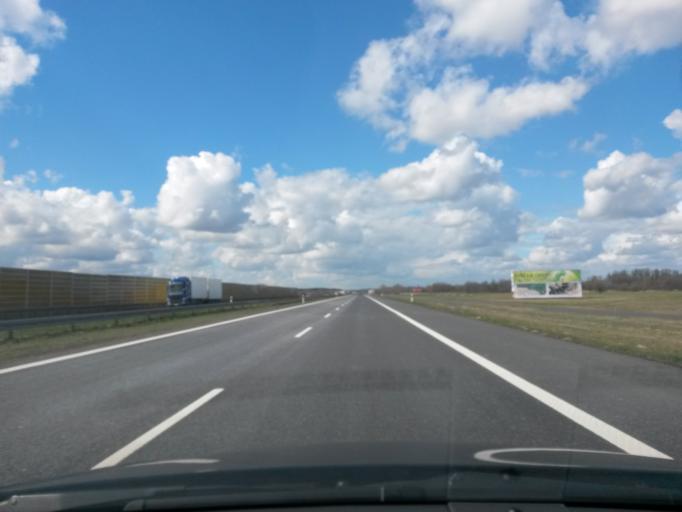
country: PL
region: Greater Poland Voivodeship
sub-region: Powiat kolski
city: Dabie
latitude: 52.0502
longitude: 18.8487
